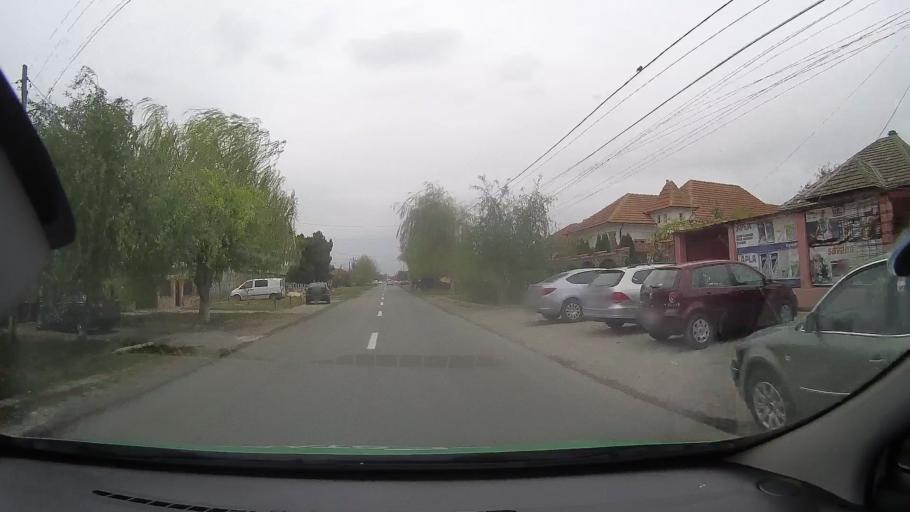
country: RO
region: Constanta
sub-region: Comuna Mihail Kogalniceanu
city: Mihail Kogalniceanu
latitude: 44.3741
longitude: 28.4644
